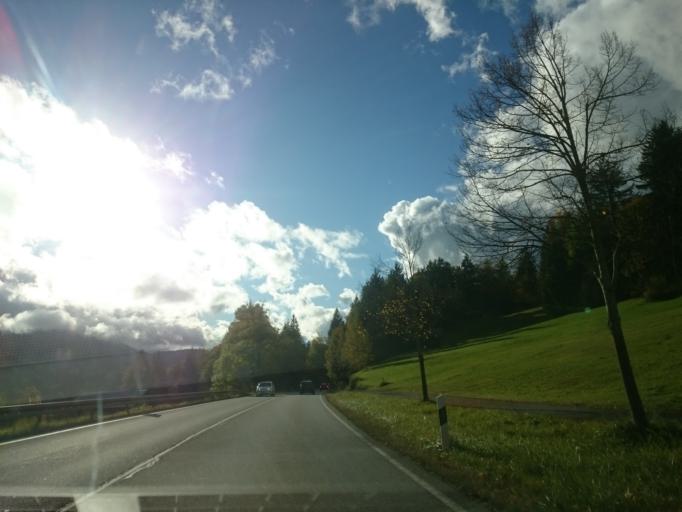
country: DE
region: Bavaria
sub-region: Upper Bavaria
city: Garmisch-Partenkirchen
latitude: 47.4878
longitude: 11.1579
